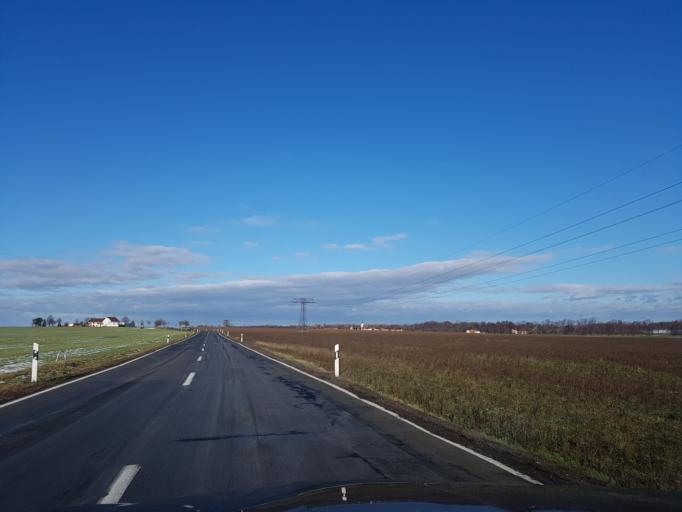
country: DE
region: Saxony
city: Priestewitz
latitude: 51.2363
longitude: 13.5551
